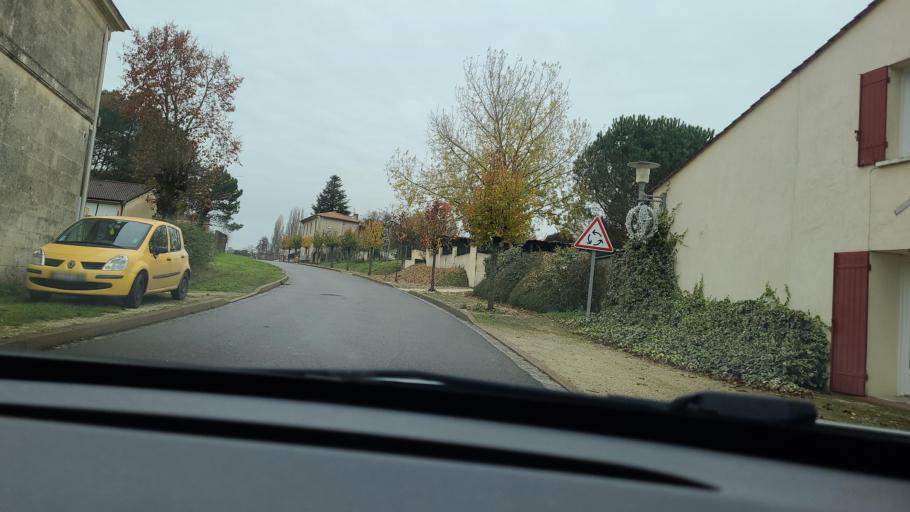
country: FR
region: Aquitaine
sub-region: Departement de la Gironde
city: Berson
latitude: 45.0958
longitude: -0.5470
